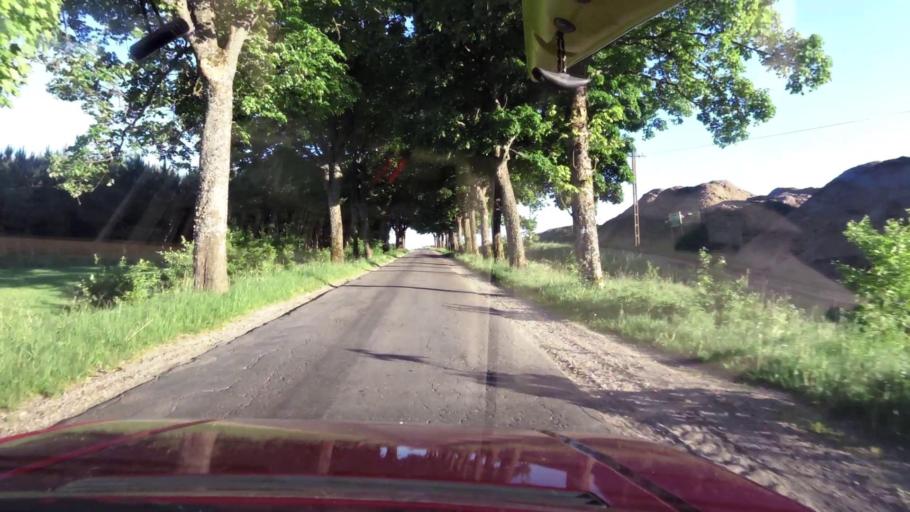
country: PL
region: West Pomeranian Voivodeship
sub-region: Powiat szczecinecki
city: Bialy Bor
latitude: 53.9407
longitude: 16.7888
